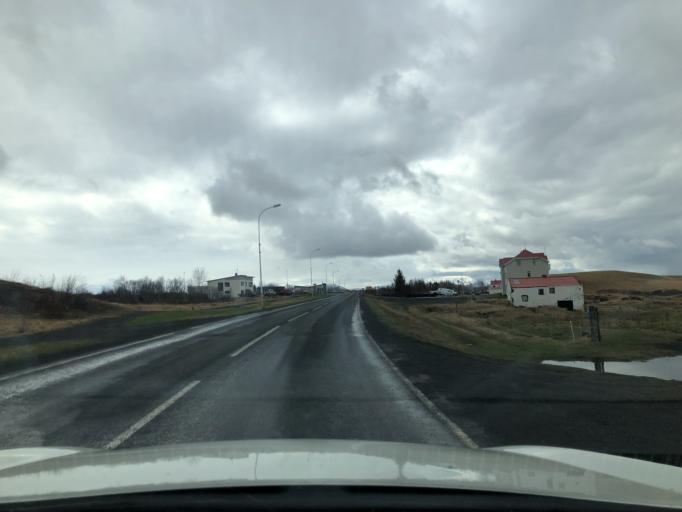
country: IS
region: Northeast
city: Laugar
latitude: 65.6438
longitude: -16.9133
